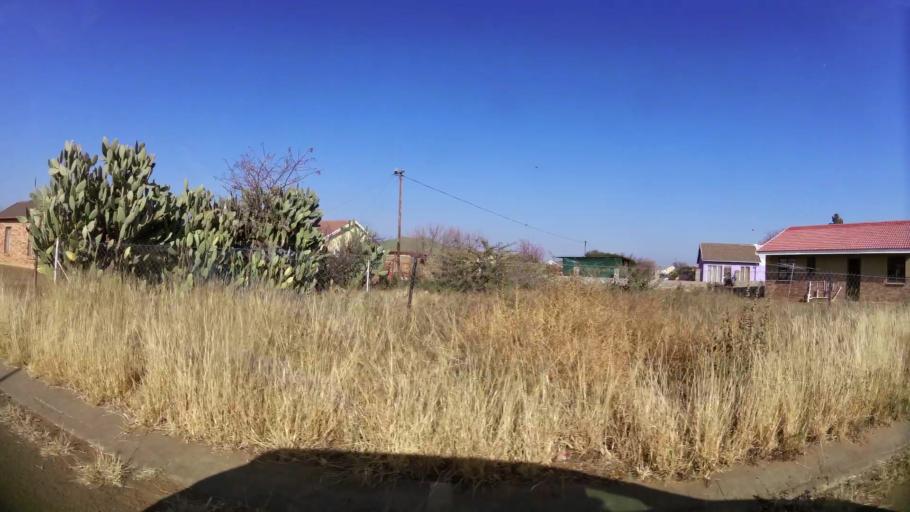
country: ZA
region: Orange Free State
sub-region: Mangaung Metropolitan Municipality
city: Bloemfontein
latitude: -29.1806
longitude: 26.1814
